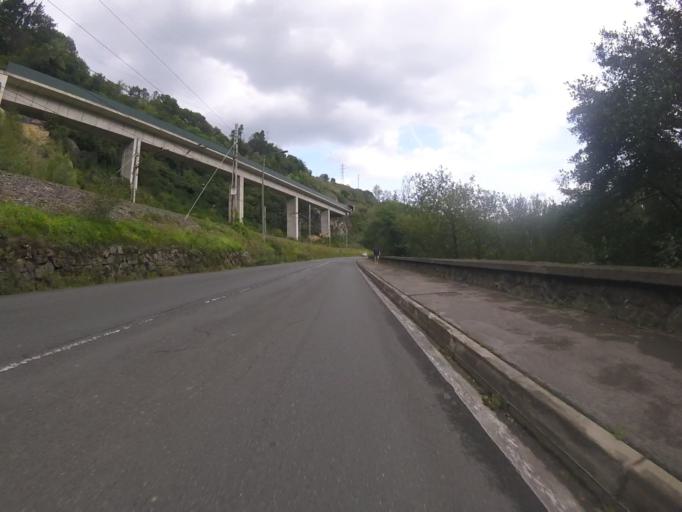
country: ES
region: Basque Country
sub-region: Provincia de Guipuzcoa
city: Tolosa
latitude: 43.1284
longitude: -2.0877
